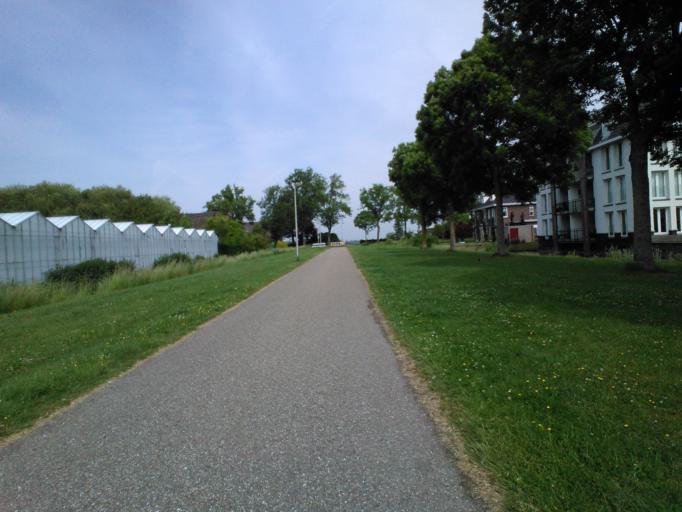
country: NL
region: South Holland
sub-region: Gemeente Waddinxveen
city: Groenswaard
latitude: 52.0345
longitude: 4.6264
